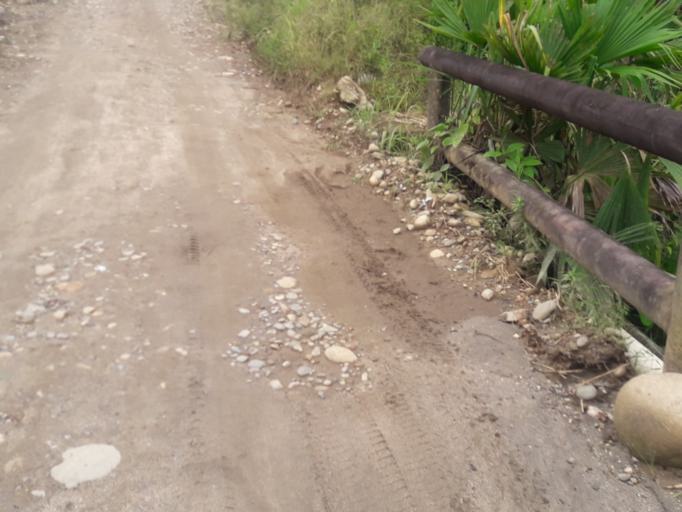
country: EC
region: Napo
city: Tena
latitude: -0.9857
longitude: -77.8276
